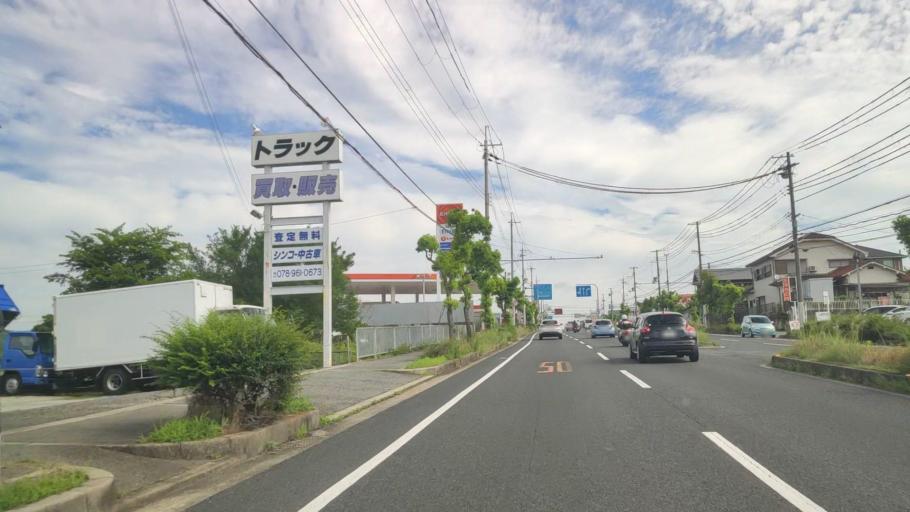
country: JP
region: Hyogo
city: Akashi
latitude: 34.6940
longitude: 134.9829
